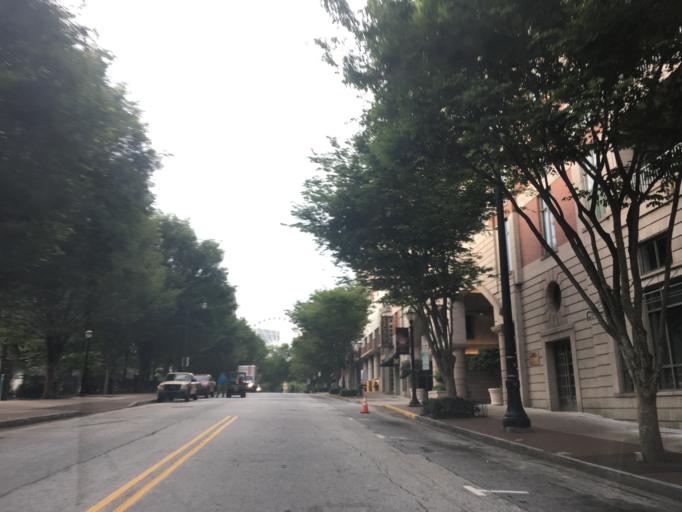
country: US
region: Georgia
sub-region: Fulton County
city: Atlanta
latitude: 33.7617
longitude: -84.3948
